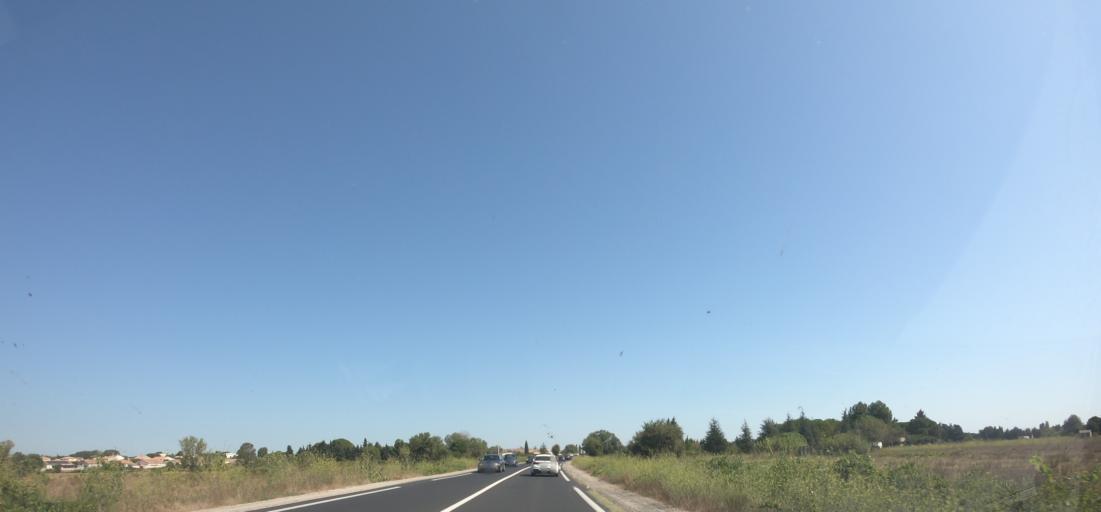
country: FR
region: Languedoc-Roussillon
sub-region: Departement de l'Herault
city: Lunel
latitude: 43.6636
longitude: 4.1390
